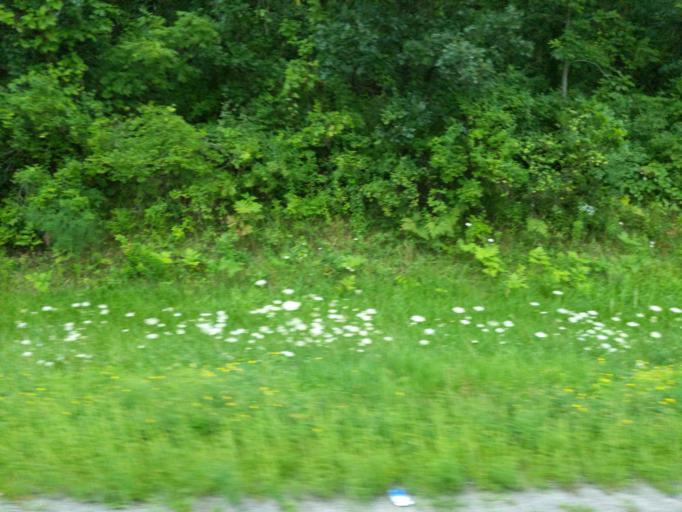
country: US
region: Wisconsin
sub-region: Sauk County
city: Sauk City
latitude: 43.2436
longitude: -89.7252
